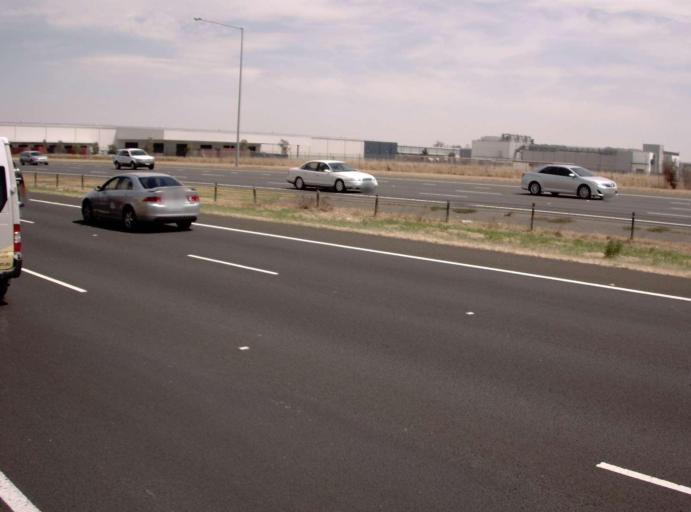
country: AU
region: Victoria
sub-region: Brimbank
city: Derrimut
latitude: -37.7874
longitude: 144.7886
